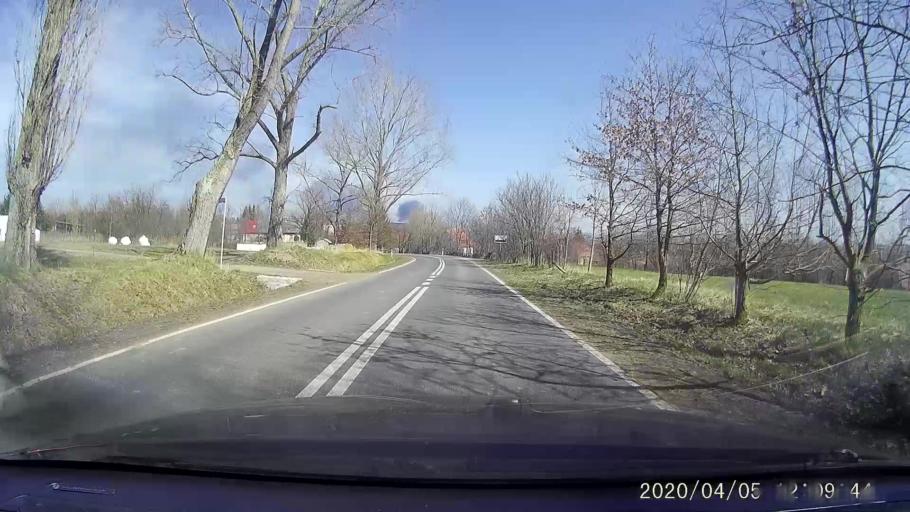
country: PL
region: Lower Silesian Voivodeship
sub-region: Powiat lwowecki
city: Mirsk
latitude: 50.9872
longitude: 15.3351
